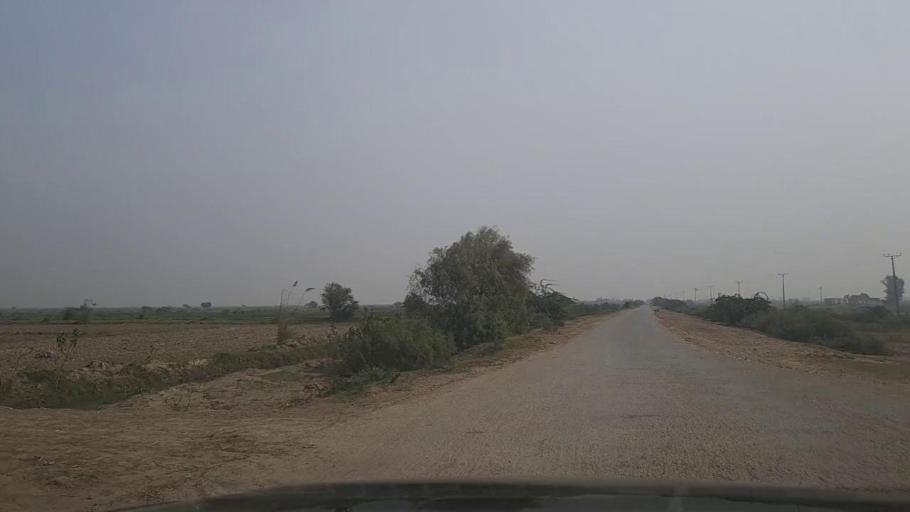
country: PK
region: Sindh
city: Mirpur Sakro
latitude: 24.4781
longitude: 67.6602
